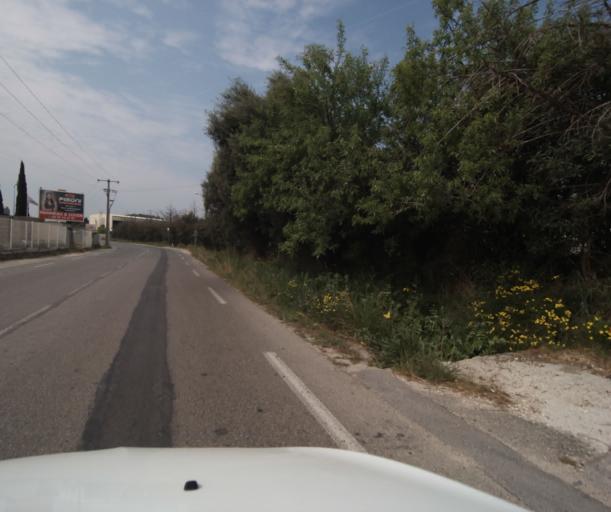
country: FR
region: Provence-Alpes-Cote d'Azur
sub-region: Departement du Var
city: La Farlede
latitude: 43.1465
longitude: 6.0346
